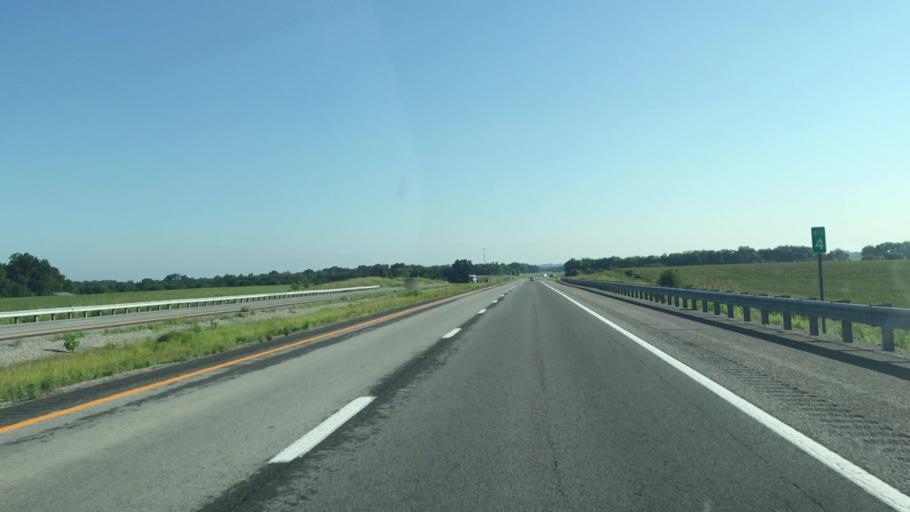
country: US
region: Kentucky
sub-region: Christian County
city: Hopkinsville
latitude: 36.7938
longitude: -87.4944
